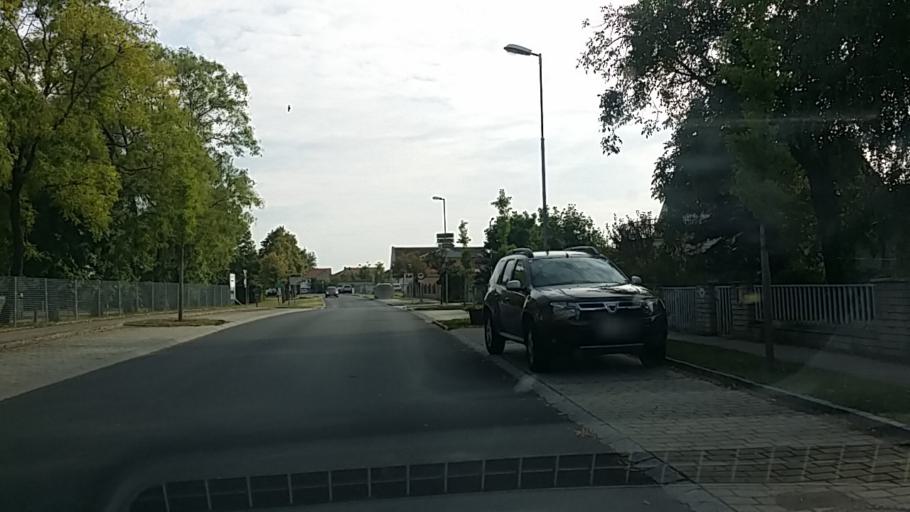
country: AT
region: Burgenland
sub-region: Eisenstadt-Umgebung
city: Sankt Margarethen im Burgenland
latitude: 47.7998
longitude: 16.6193
